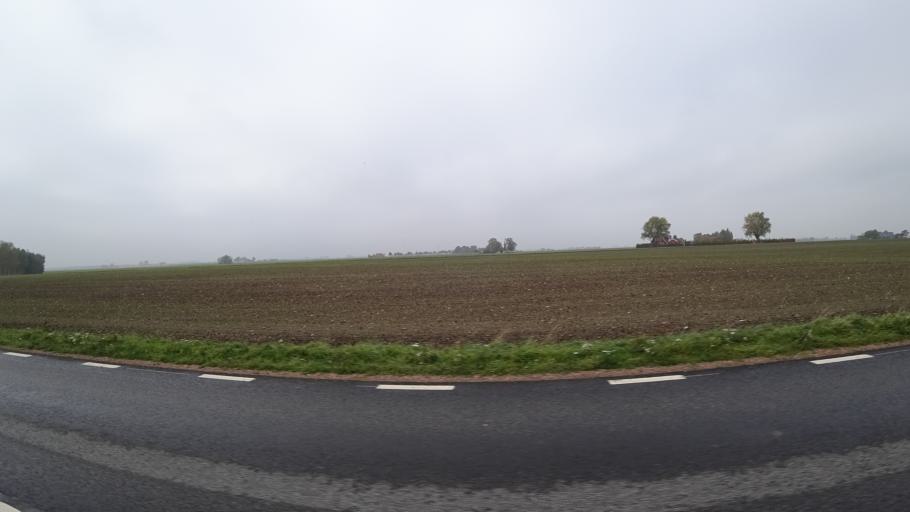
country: SE
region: Skane
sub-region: Kavlinge Kommun
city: Loddekopinge
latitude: 55.7739
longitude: 13.0589
